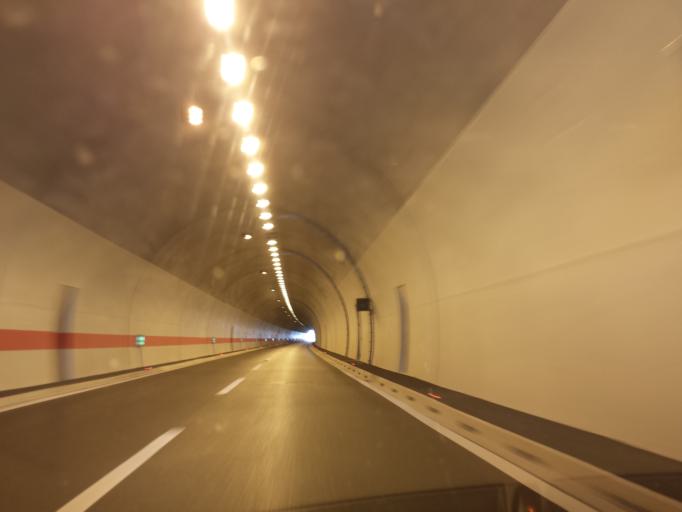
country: BA
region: Federation of Bosnia and Herzegovina
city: Capljina
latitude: 43.1552
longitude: 17.6292
